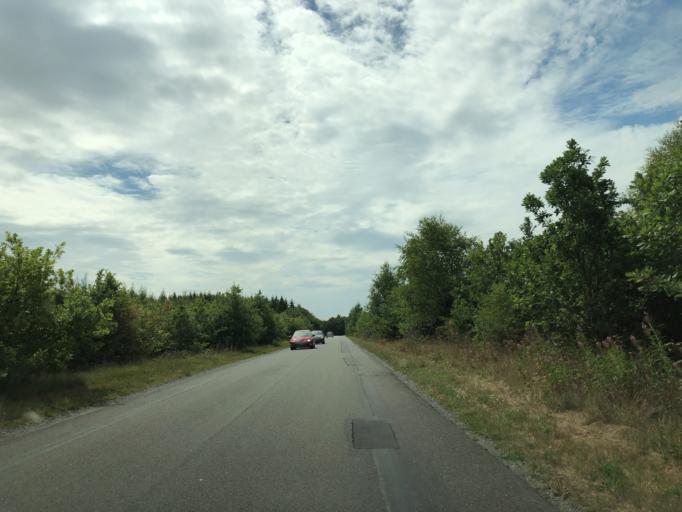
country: DK
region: South Denmark
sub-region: Vejle Kommune
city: Egtved
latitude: 55.6296
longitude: 9.1949
